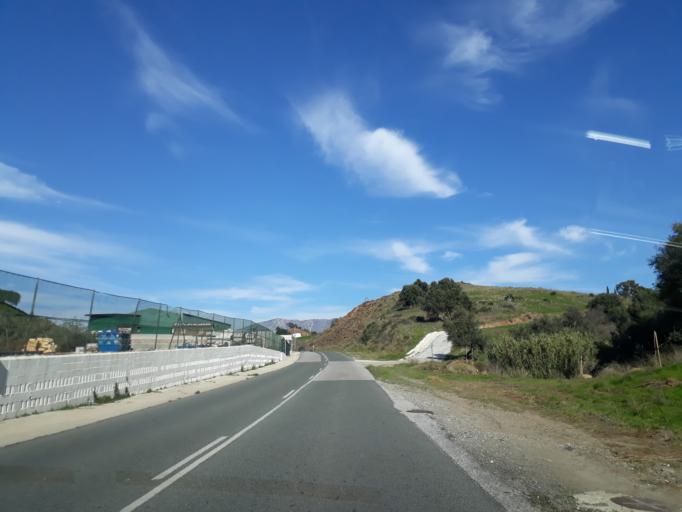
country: ES
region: Andalusia
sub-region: Provincia de Malaga
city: Fuengirola
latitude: 36.5174
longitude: -4.6847
